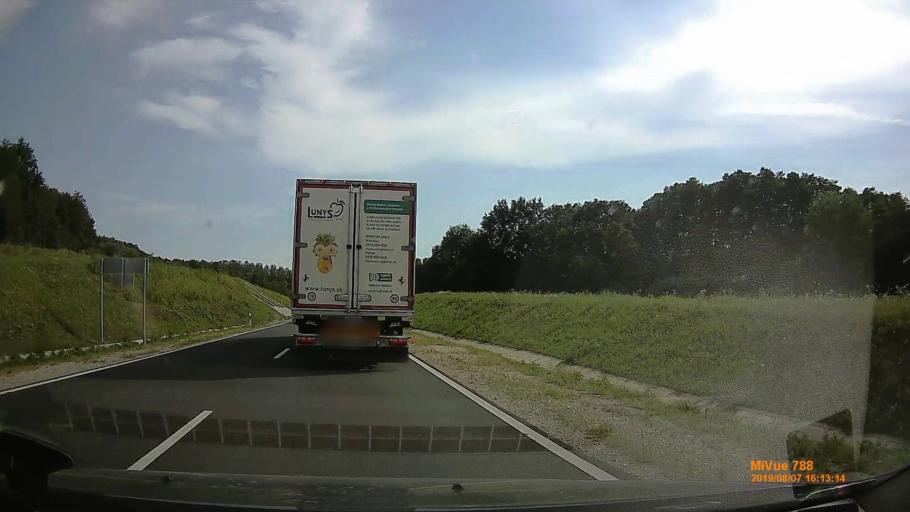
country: HU
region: Zala
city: Zalalovo
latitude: 46.8453
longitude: 16.6292
